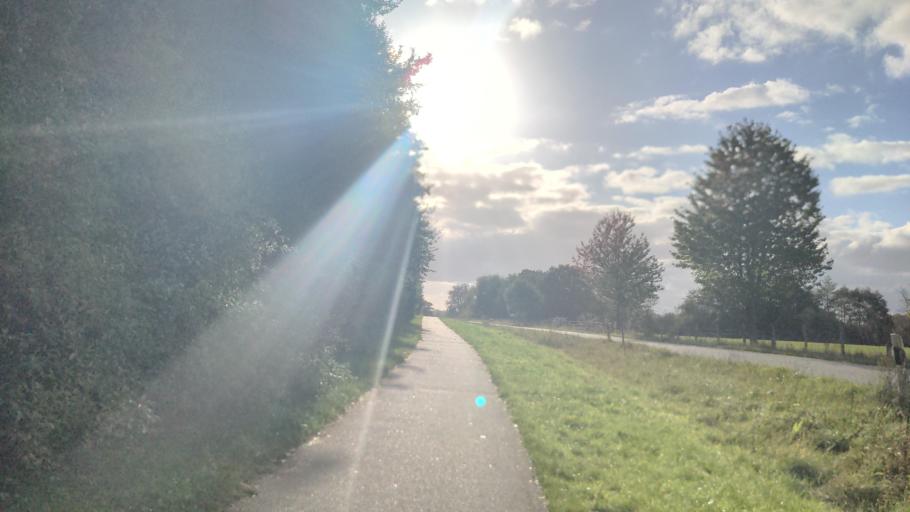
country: DE
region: Schleswig-Holstein
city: Bosau
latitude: 54.1286
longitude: 10.4515
